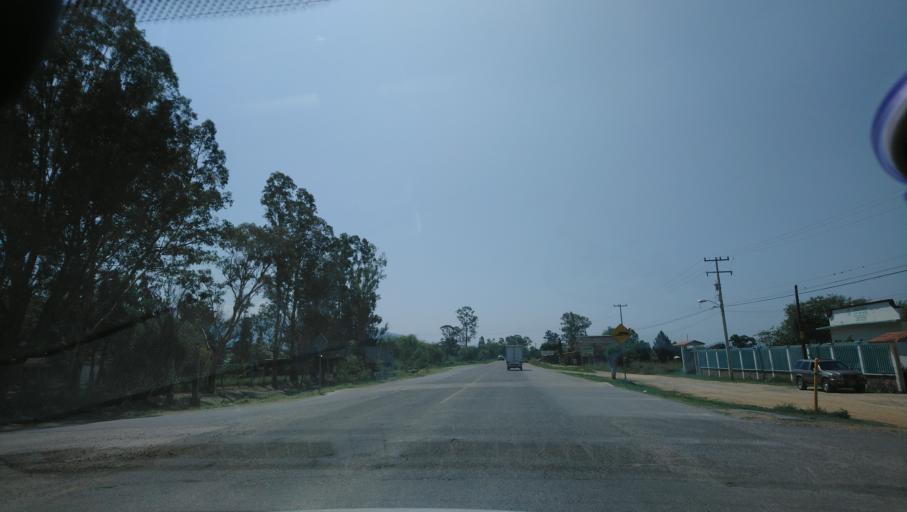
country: MX
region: Oaxaca
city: Santa Maria del Tule
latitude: 17.0438
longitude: -96.6308
